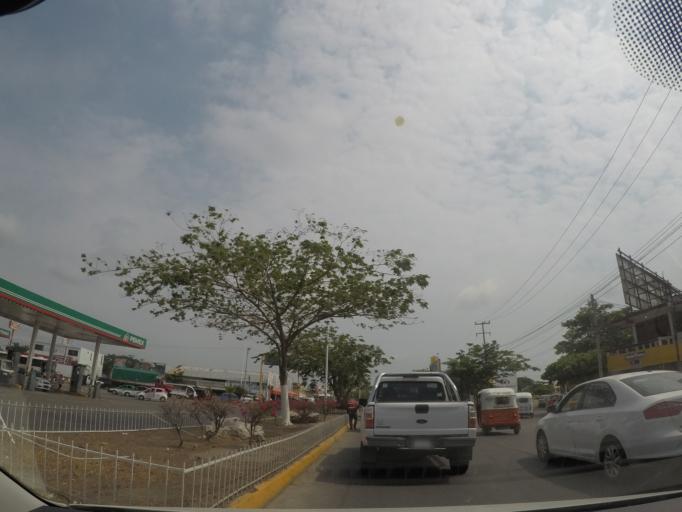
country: MX
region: Oaxaca
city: Juchitan de Zaragoza
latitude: 16.4457
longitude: -95.0250
